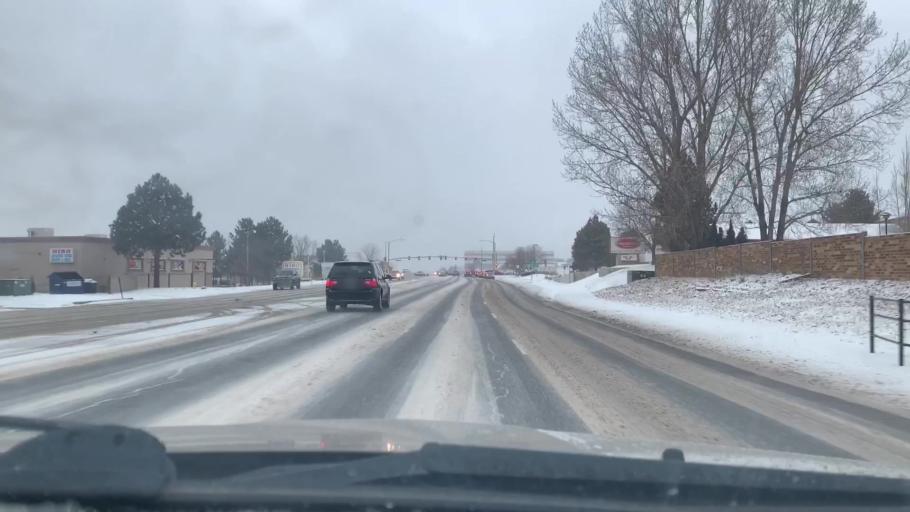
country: US
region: Colorado
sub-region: Adams County
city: Aurora
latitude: 39.6657
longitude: -104.8603
